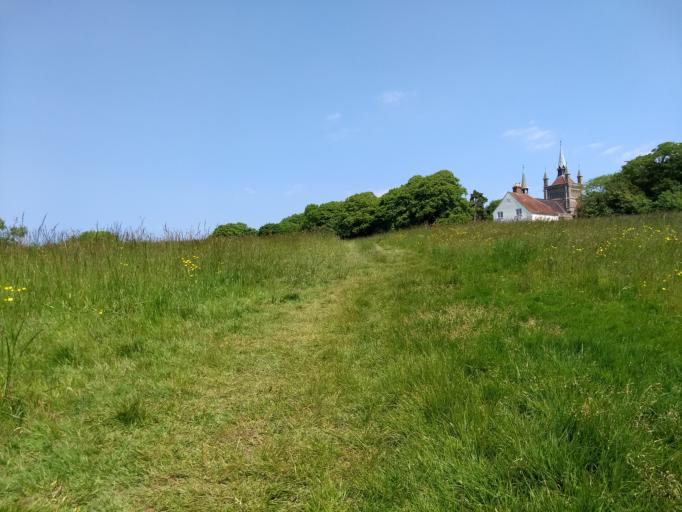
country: GB
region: England
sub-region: Isle of Wight
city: East Cowes
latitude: 50.7388
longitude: -1.2784
